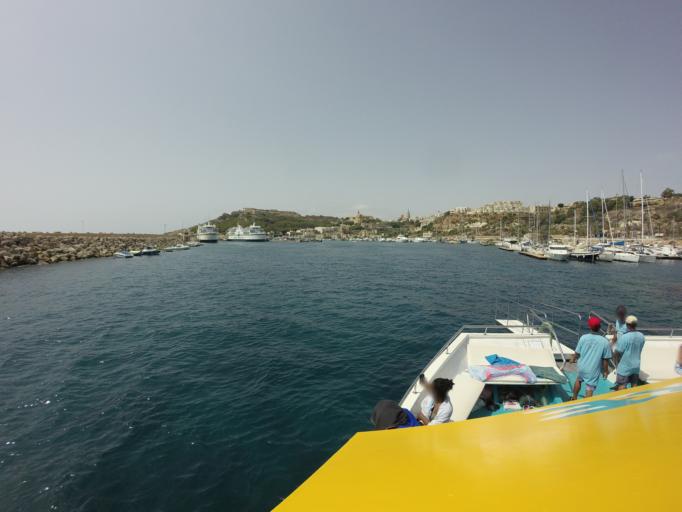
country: MT
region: Ghajnsielem
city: Mgarr
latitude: 36.0257
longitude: 14.3021
